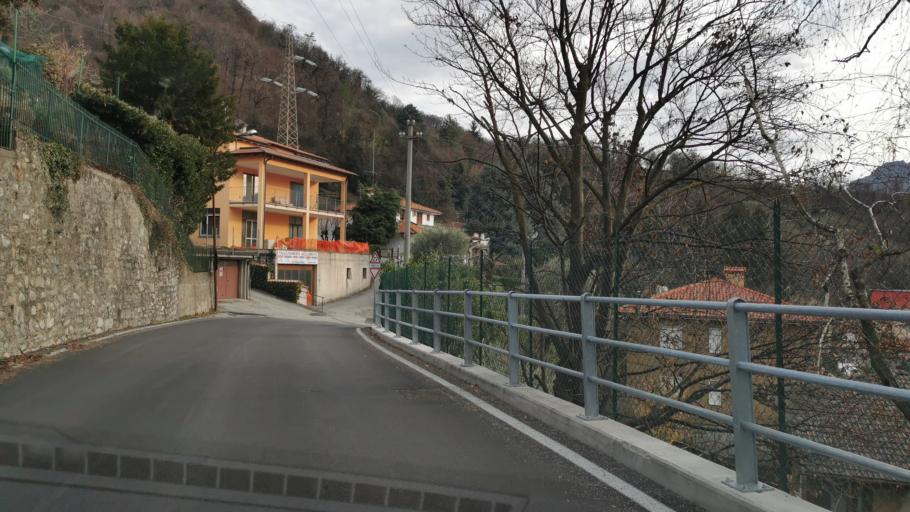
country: IT
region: Lombardy
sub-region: Provincia di Lecco
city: Mandello del Lario
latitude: 45.9219
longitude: 9.3273
